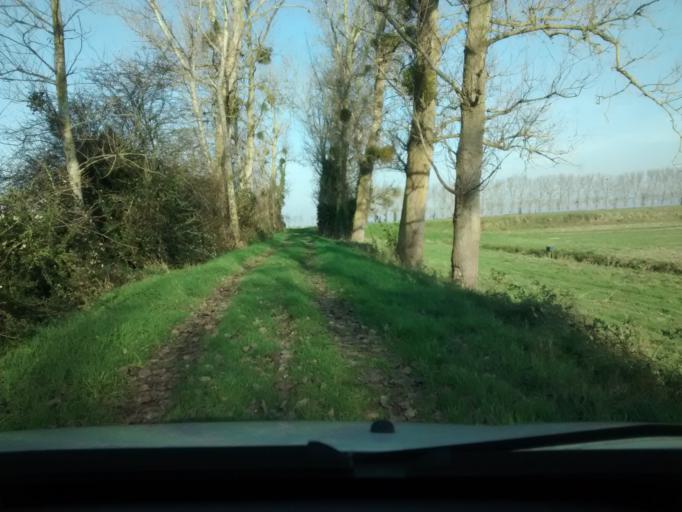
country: FR
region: Brittany
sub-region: Departement d'Ille-et-Vilaine
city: Roz-sur-Couesnon
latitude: 48.6111
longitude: -1.5935
